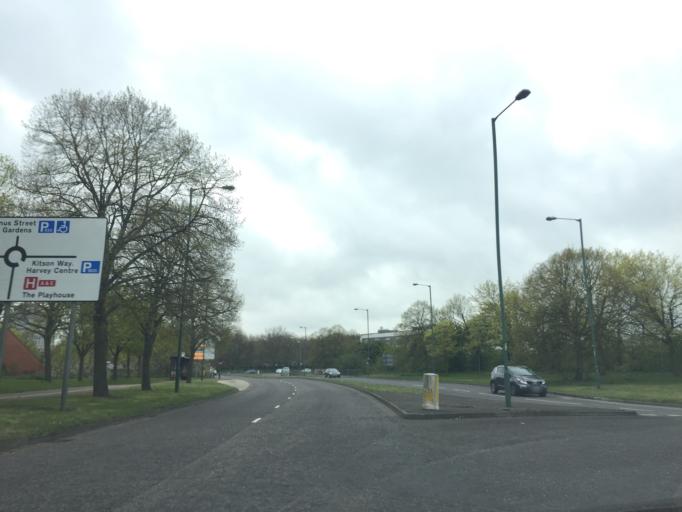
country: GB
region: England
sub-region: Essex
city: Harlow
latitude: 51.7746
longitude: 0.0961
